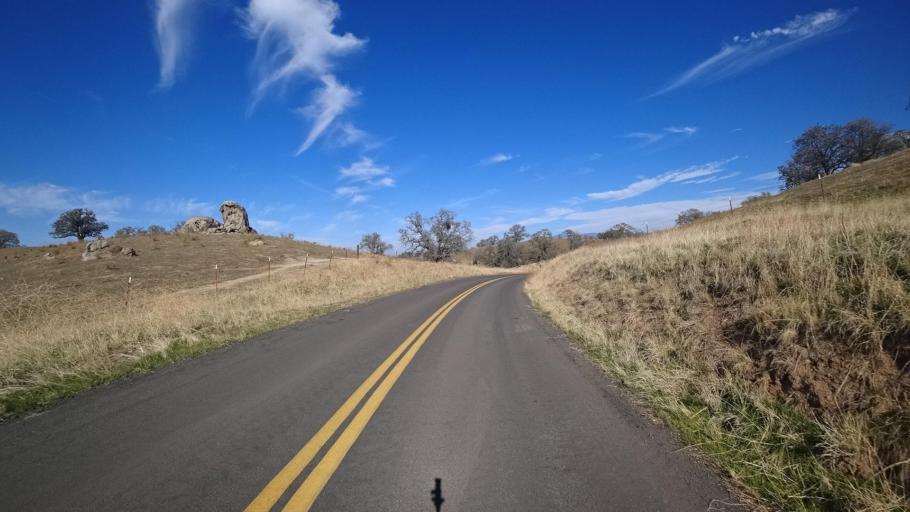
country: US
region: California
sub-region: Kern County
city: Oildale
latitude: 35.6227
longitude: -118.8500
